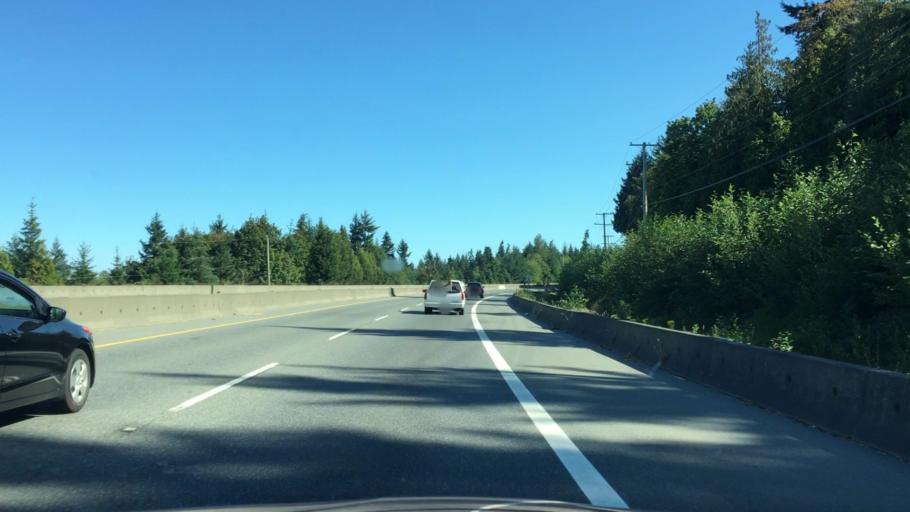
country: CA
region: British Columbia
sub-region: Cowichan Valley Regional District
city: Ladysmith
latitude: 48.9633
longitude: -123.7827
